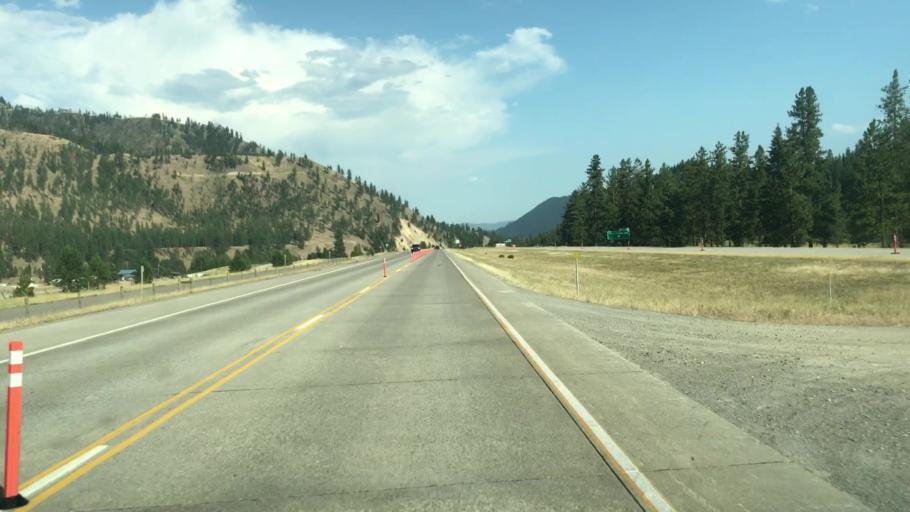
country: US
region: Montana
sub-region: Mineral County
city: Superior
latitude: 47.2297
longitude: -114.9769
